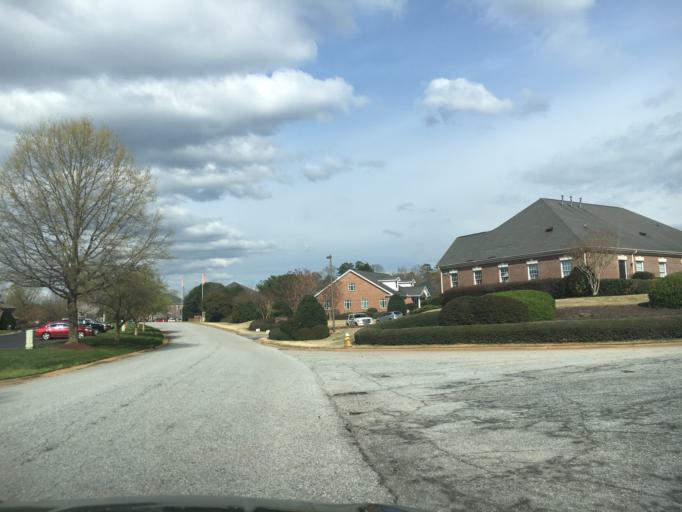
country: US
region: South Carolina
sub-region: Greenville County
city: Taylors
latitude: 34.8624
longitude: -82.2723
